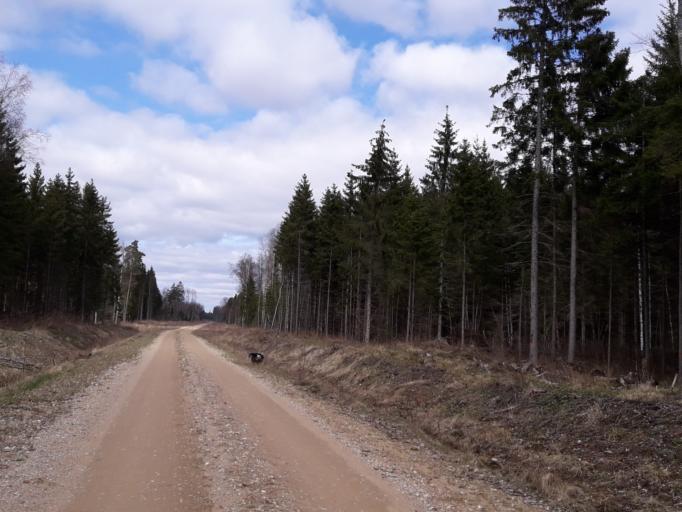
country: LV
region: Talsu Rajons
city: Sabile
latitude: 56.8926
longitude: 22.3805
